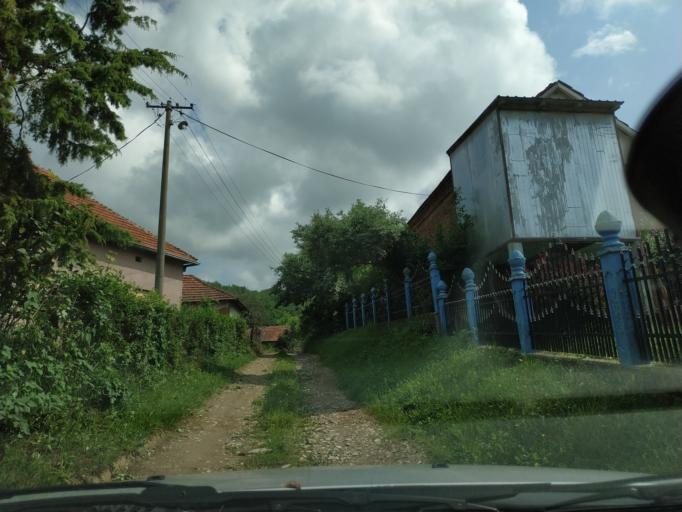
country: RS
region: Central Serbia
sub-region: Nisavski Okrug
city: Aleksinac
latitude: 43.4245
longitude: 21.5843
